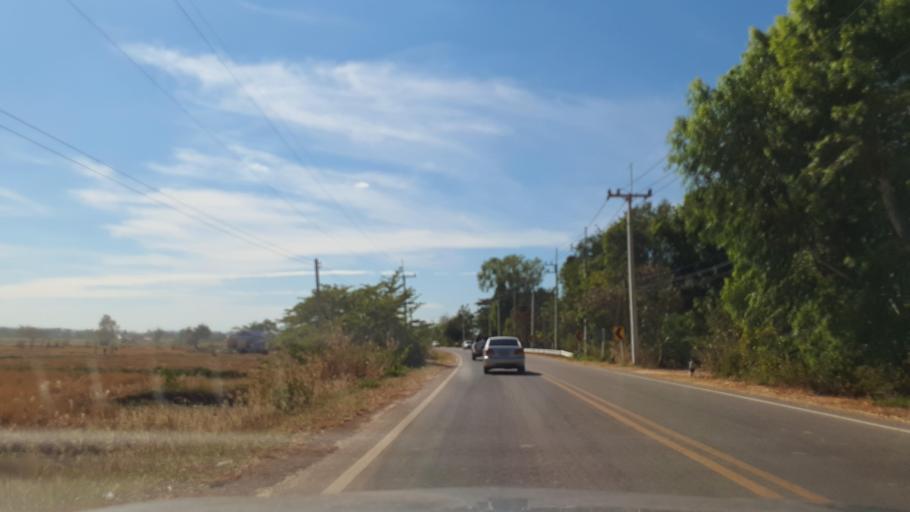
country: TH
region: Kalasin
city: Khao Wong
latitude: 16.7472
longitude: 104.1149
